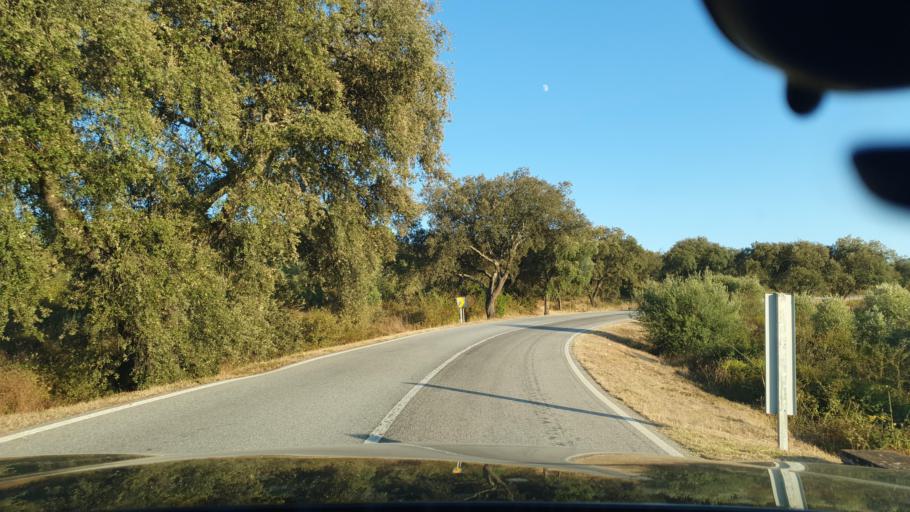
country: PT
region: Evora
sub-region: Estremoz
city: Estremoz
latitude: 38.9140
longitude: -7.6629
